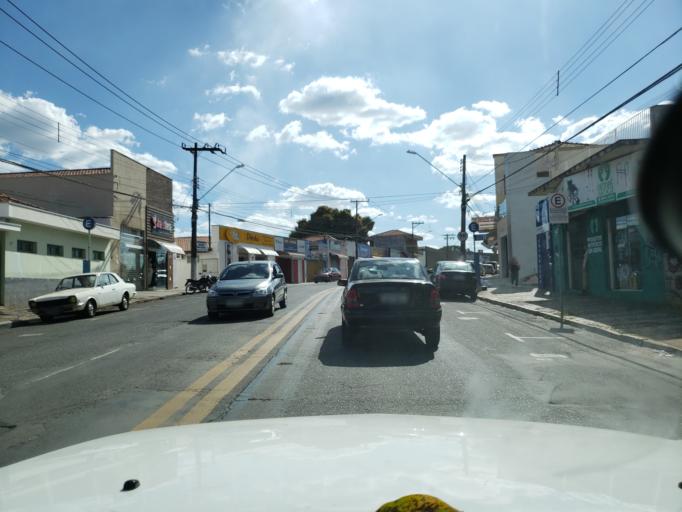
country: BR
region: Sao Paulo
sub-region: Moji-Guacu
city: Mogi-Gaucu
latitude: -22.3705
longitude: -46.9444
